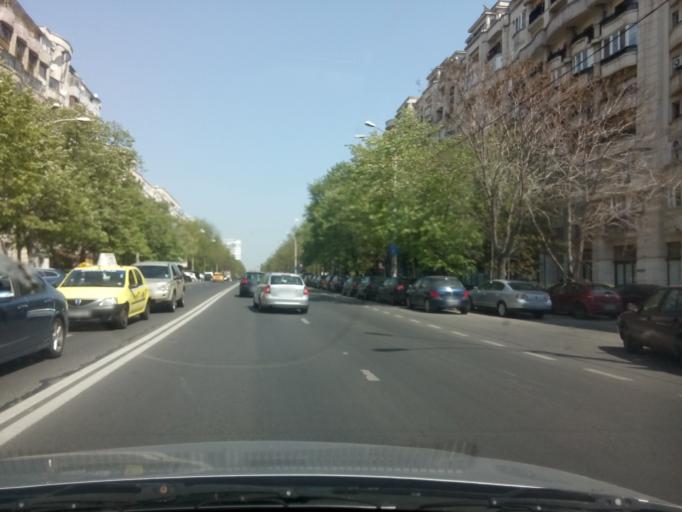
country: RO
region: Bucuresti
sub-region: Municipiul Bucuresti
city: Bucharest
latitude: 44.4267
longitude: 26.1299
